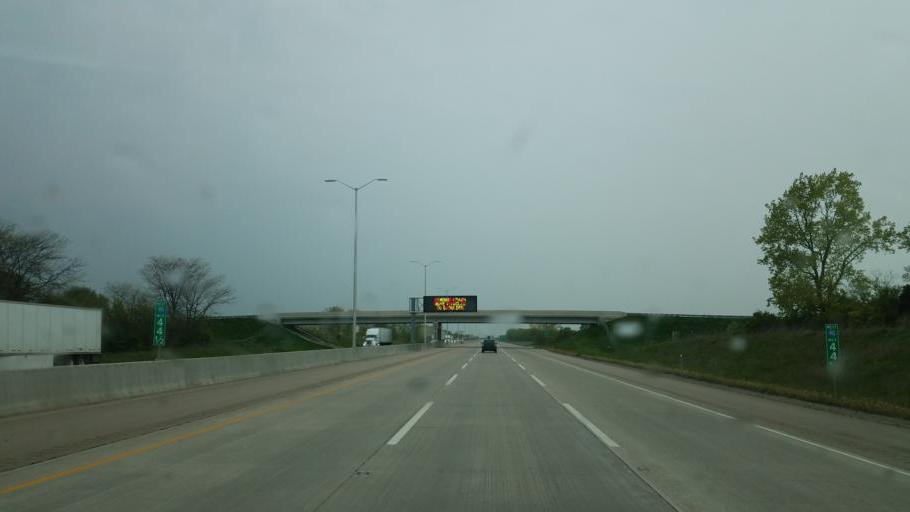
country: US
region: Illinois
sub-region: McHenry County
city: Huntley
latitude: 42.1327
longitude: -88.4664
